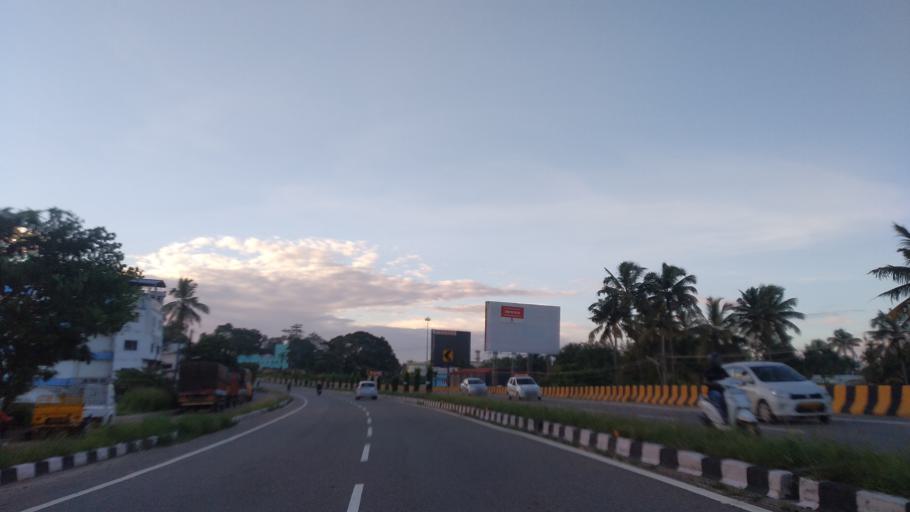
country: IN
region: Kerala
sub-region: Ernakulam
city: Elur
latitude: 10.0691
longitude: 76.3215
